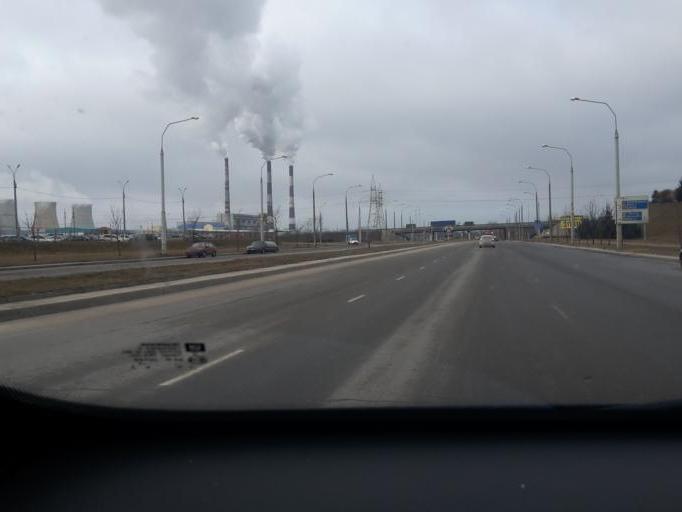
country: BY
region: Minsk
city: Malinovka
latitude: 53.8801
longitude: 27.4242
